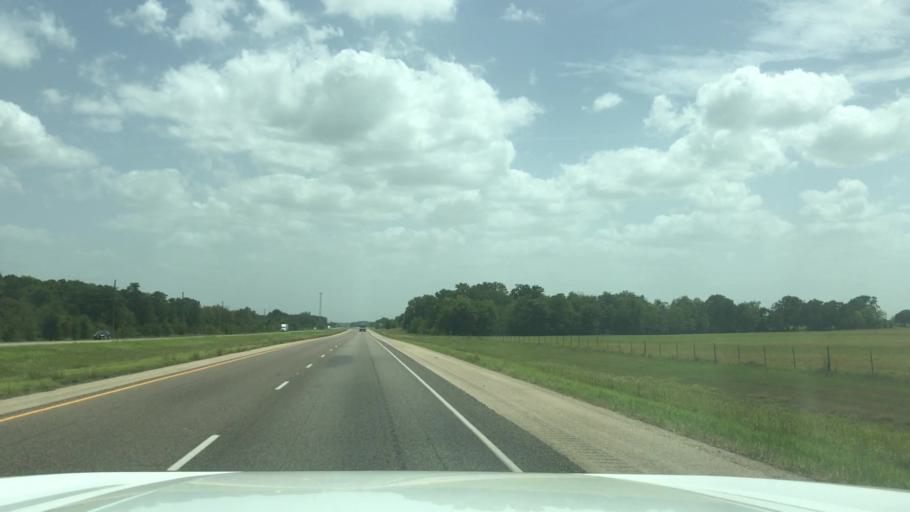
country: US
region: Texas
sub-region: Robertson County
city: Calvert
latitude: 31.0464
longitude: -96.7109
